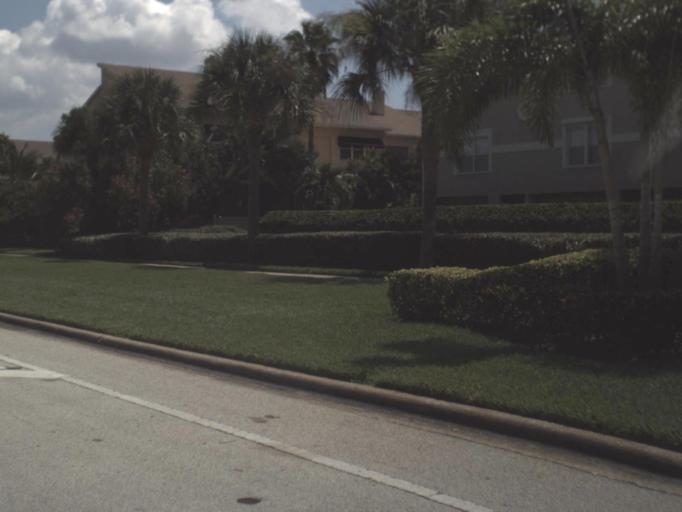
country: US
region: Florida
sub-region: Pinellas County
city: Tierra Verde
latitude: 27.6844
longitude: -82.7237
